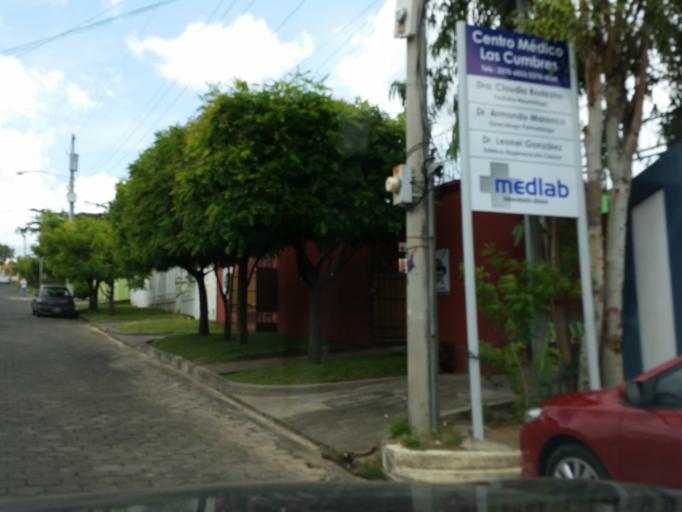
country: NI
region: Managua
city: Managua
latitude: 12.1021
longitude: -86.2572
